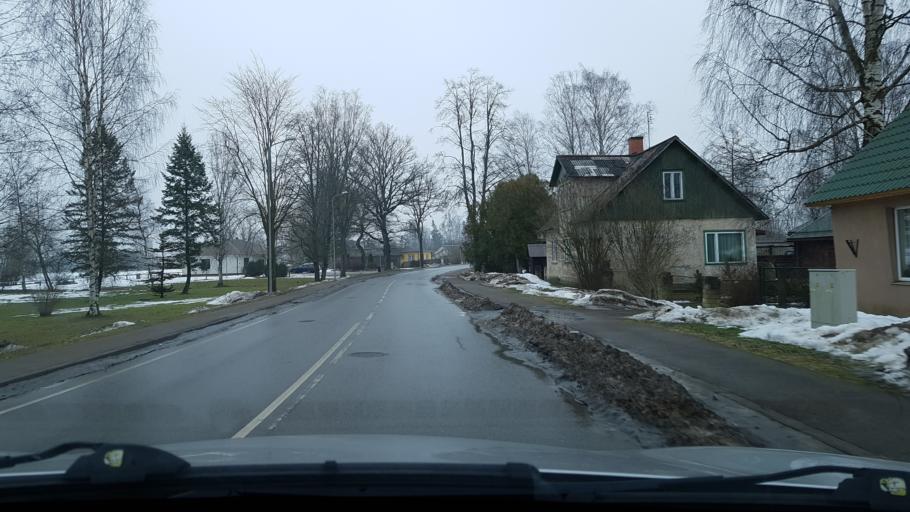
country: EE
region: Valgamaa
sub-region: Torva linn
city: Torva
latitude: 58.2348
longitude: 25.8682
